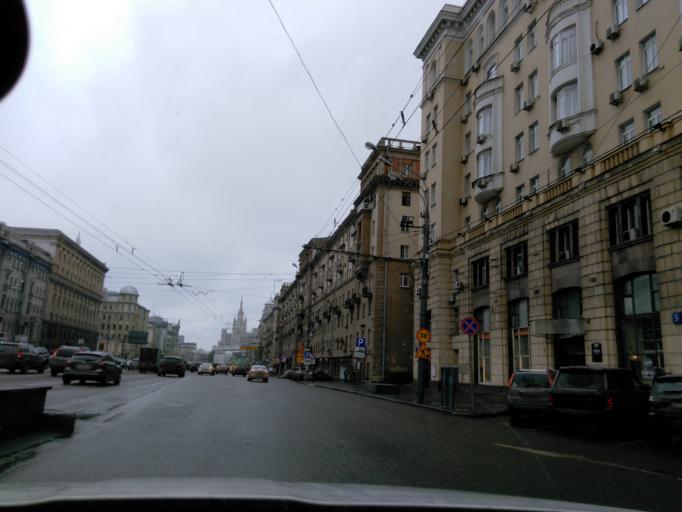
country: RU
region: Moscow
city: Moscow
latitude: 55.7683
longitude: 37.5938
